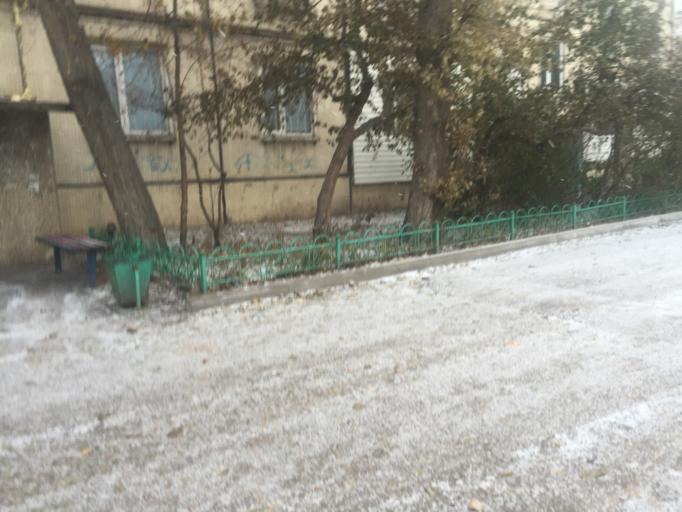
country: KZ
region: Astana Qalasy
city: Astana
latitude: 51.1872
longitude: 71.4145
